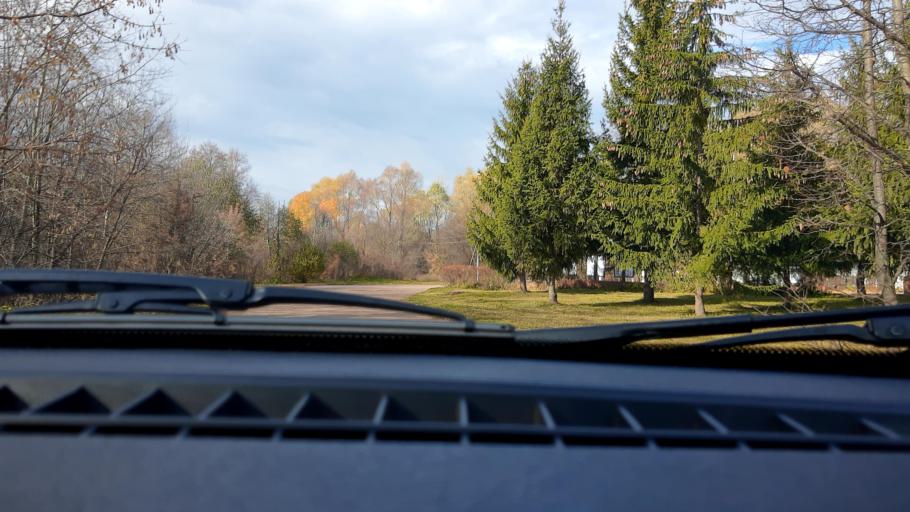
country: RU
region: Bashkortostan
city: Mikhaylovka
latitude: 54.8053
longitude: 55.8321
